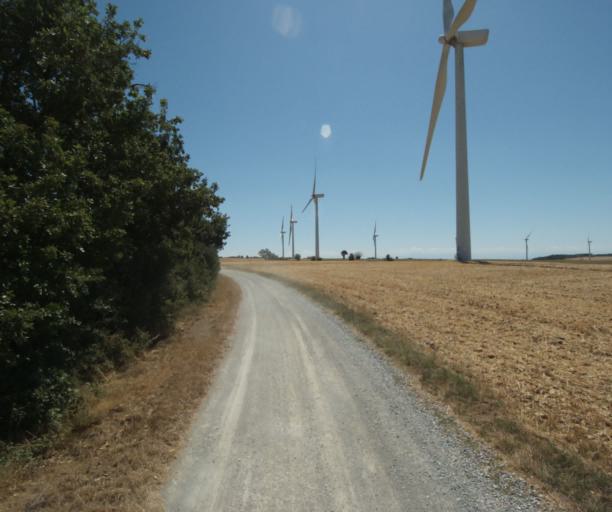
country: FR
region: Midi-Pyrenees
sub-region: Departement de la Haute-Garonne
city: Saint-Felix-Lauragais
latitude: 43.4692
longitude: 1.9182
